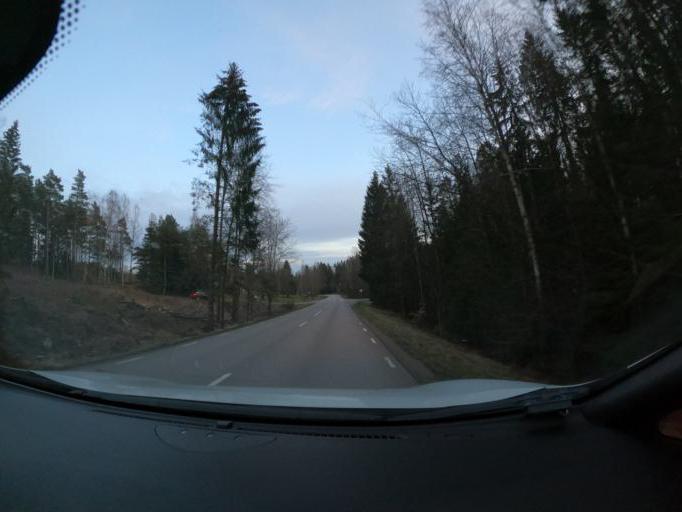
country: SE
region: Vaestra Goetaland
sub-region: Harryda Kommun
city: Molnlycke
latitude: 57.6447
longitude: 12.1606
